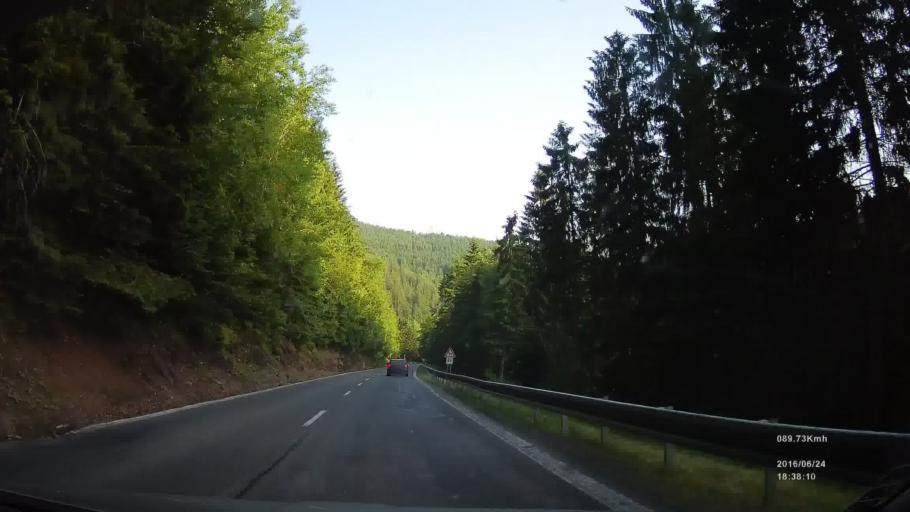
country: SK
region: Banskobystricky
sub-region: Okres Banska Bystrica
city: Brezno
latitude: 48.8968
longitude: 19.7012
